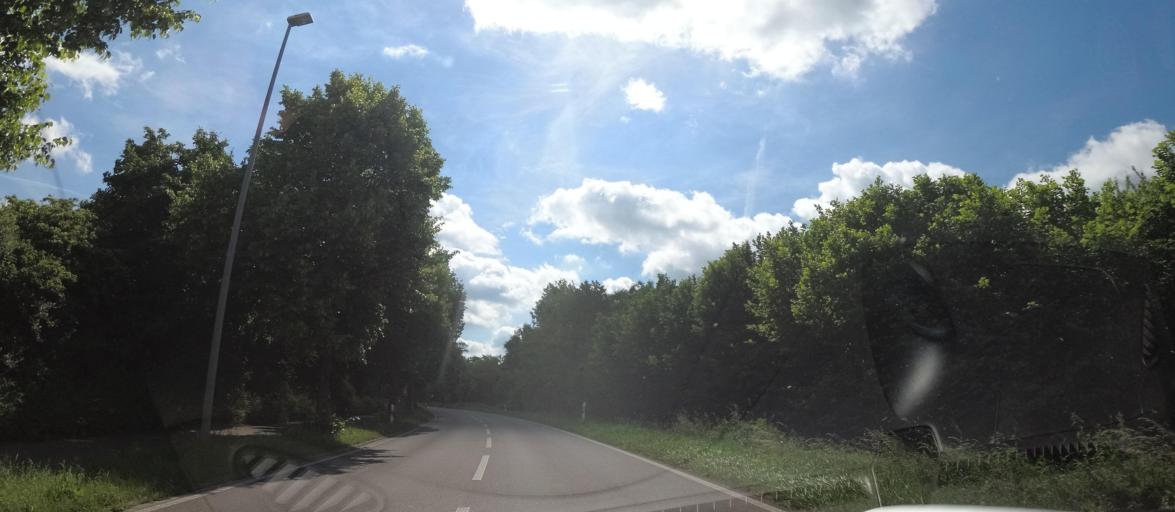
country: DE
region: Baden-Wuerttemberg
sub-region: Karlsruhe Region
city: Weingarten
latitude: 49.0888
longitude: 8.5412
